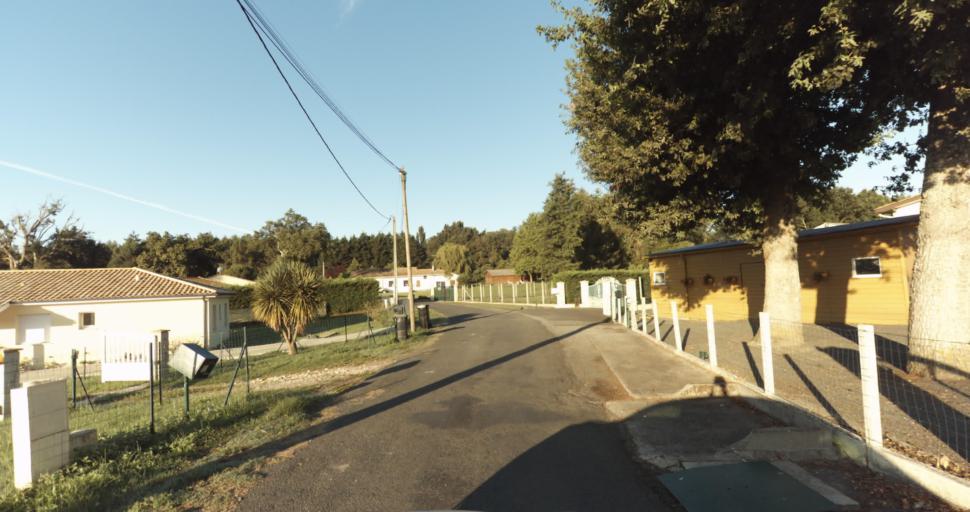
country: FR
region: Aquitaine
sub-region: Departement de la Gironde
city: Bazas
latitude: 44.4343
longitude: -0.2365
